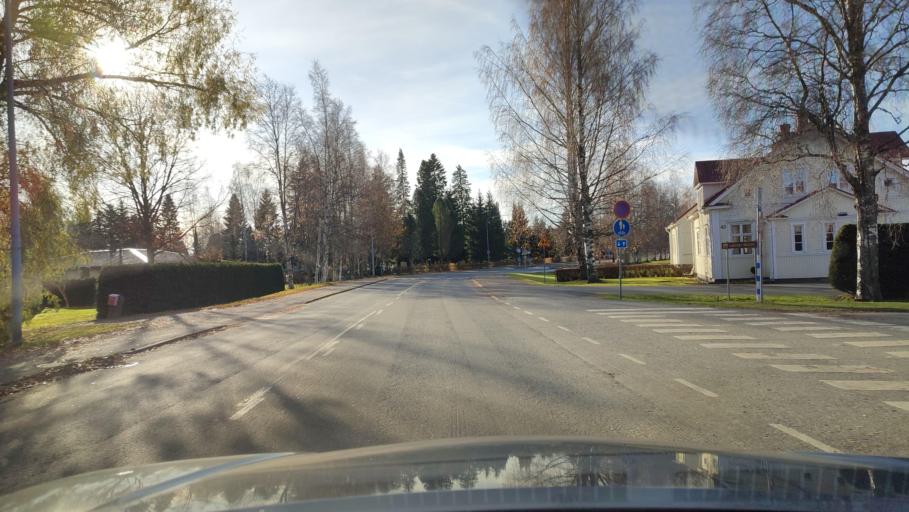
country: FI
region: Southern Ostrobothnia
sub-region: Suupohja
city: Teuva
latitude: 62.4824
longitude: 21.7437
